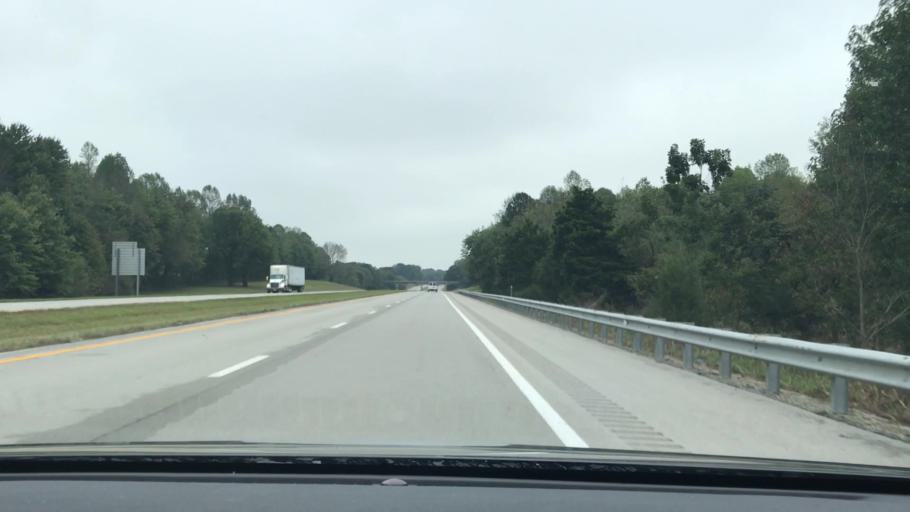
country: US
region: Kentucky
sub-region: Pulaski County
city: Somerset
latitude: 37.0962
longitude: -84.7807
